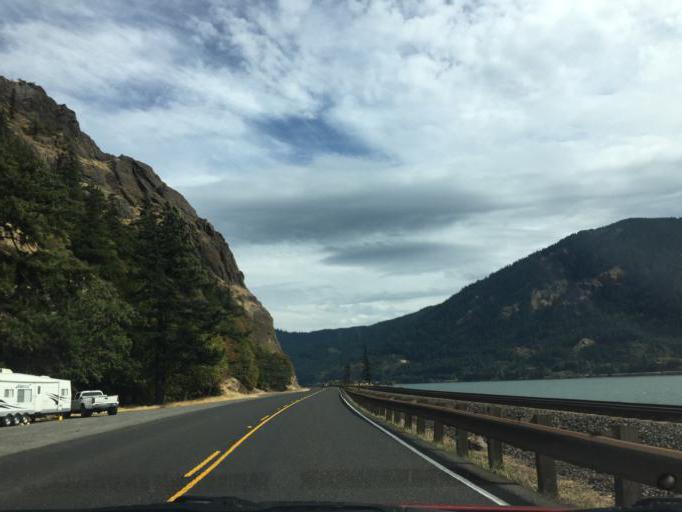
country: US
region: Washington
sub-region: Skamania County
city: Carson
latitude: 45.7099
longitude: -121.6708
